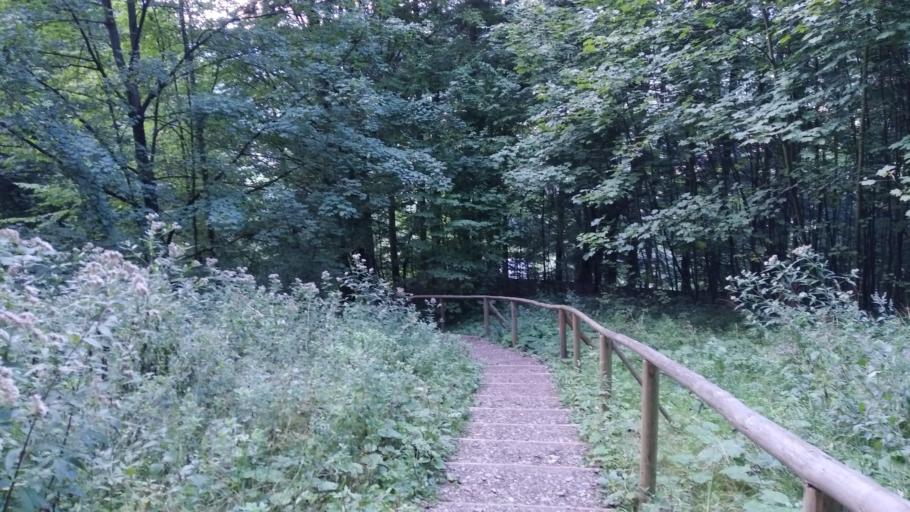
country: PL
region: Lesser Poland Voivodeship
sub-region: Powiat nowotarski
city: Kroscienko nad Dunajcem
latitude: 49.4219
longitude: 20.4434
